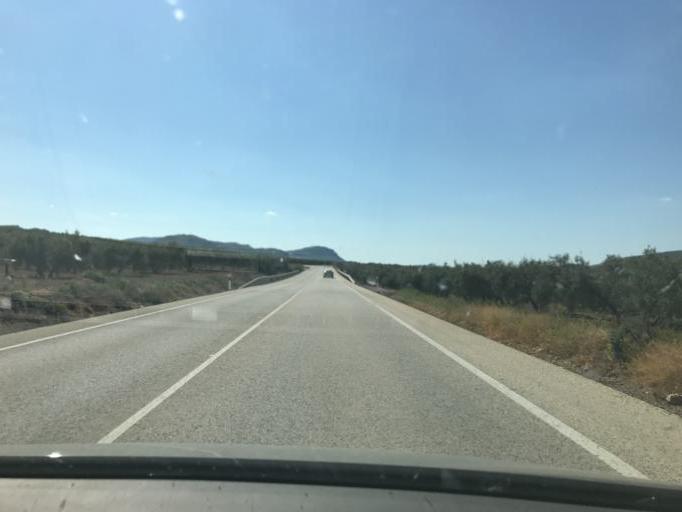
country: ES
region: Andalusia
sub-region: Province of Cordoba
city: Luque
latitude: 37.5636
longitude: -4.2082
